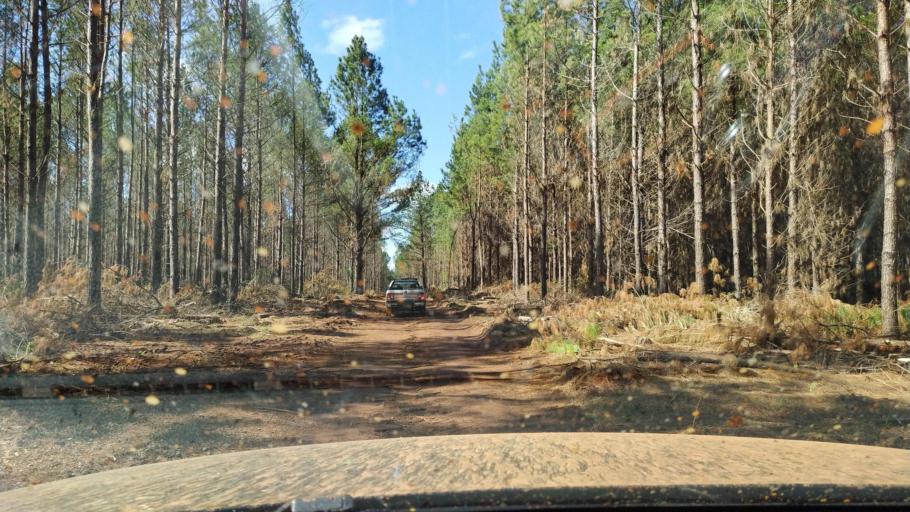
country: AR
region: Corrientes
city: Santo Tome
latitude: -28.4086
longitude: -56.0157
